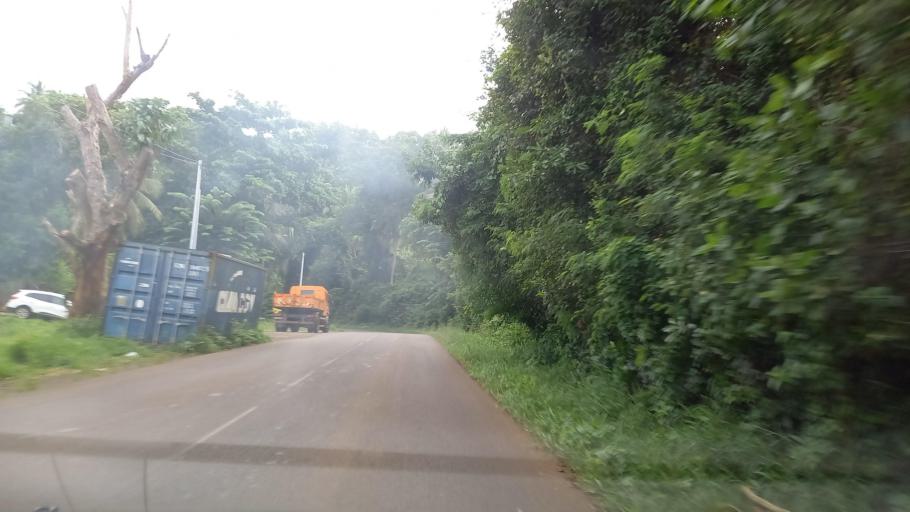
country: YT
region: Sada
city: Sada
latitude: -12.8538
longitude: 45.1049
